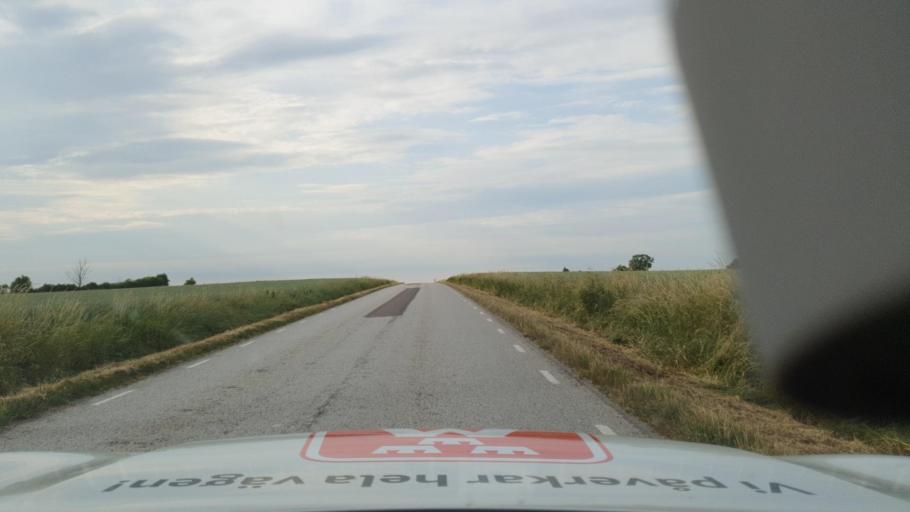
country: SE
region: Skane
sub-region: Sjobo Kommun
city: Sjoebo
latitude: 55.6488
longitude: 13.8143
